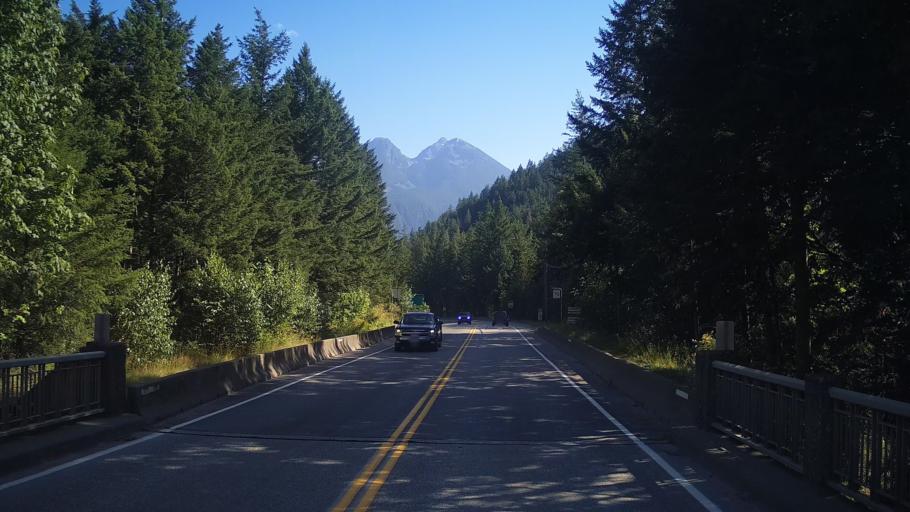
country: CA
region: British Columbia
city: Hope
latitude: 49.3903
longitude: -121.4611
